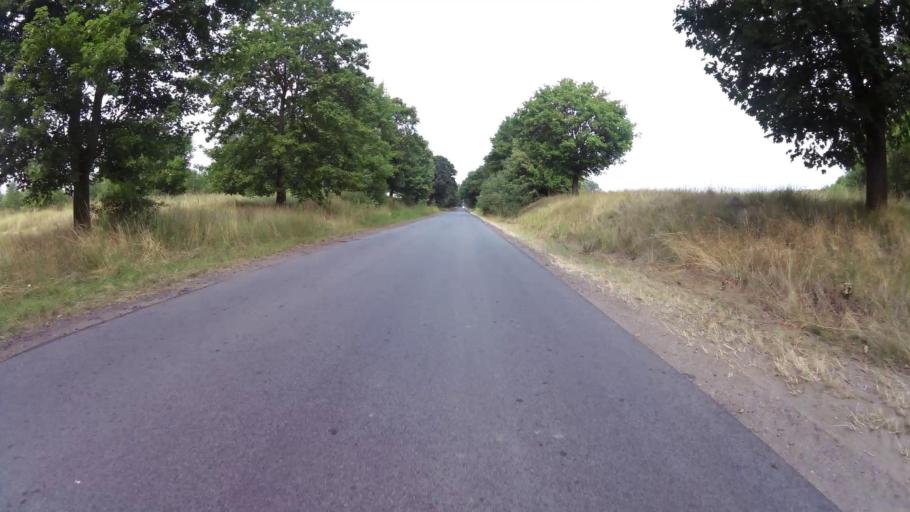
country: PL
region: West Pomeranian Voivodeship
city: Trzcinsko Zdroj
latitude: 52.9557
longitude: 14.6250
